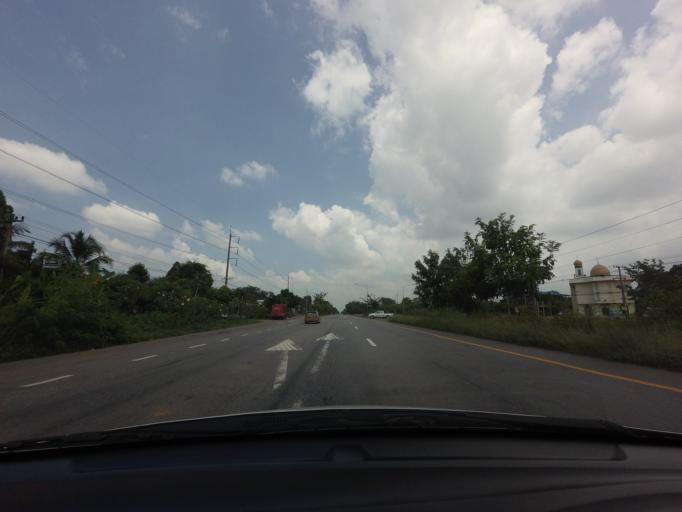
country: TH
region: Prachin Buri
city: Kabin Buri
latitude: 13.9436
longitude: 101.7074
